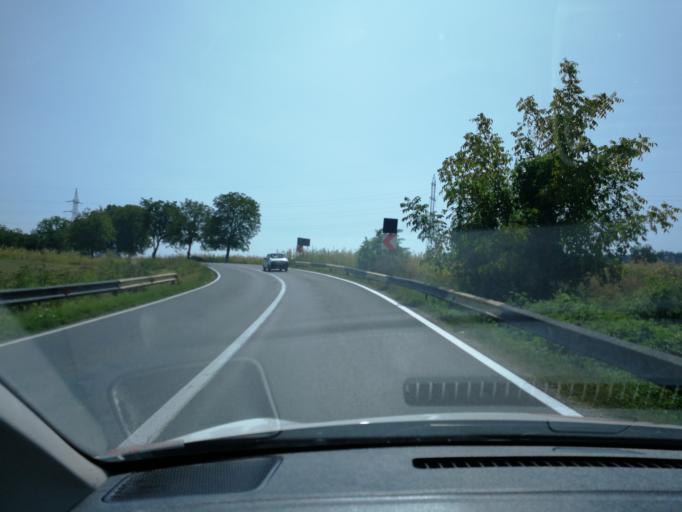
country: RO
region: Prahova
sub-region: Comuna Izvoarele
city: Homoraciu
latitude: 45.2479
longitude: 26.0237
